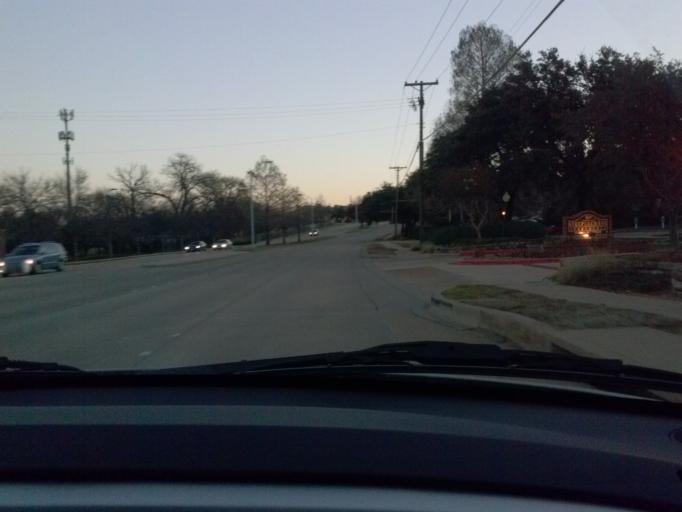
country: US
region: Texas
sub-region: Collin County
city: Allen
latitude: 33.0752
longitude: -96.7103
